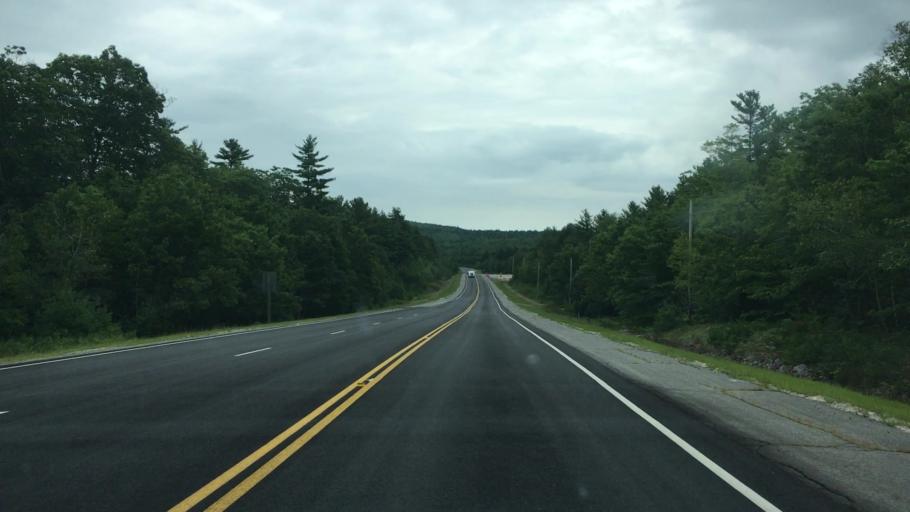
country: US
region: Maine
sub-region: Washington County
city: Cherryfield
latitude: 44.8781
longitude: -67.8748
